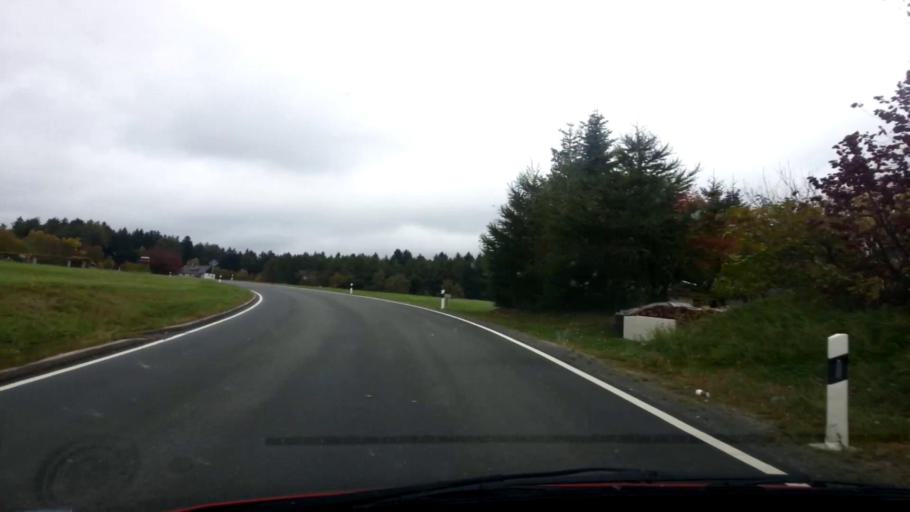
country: DE
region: Bavaria
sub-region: Upper Franconia
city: Fichtelberg
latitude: 49.9996
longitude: 11.8571
